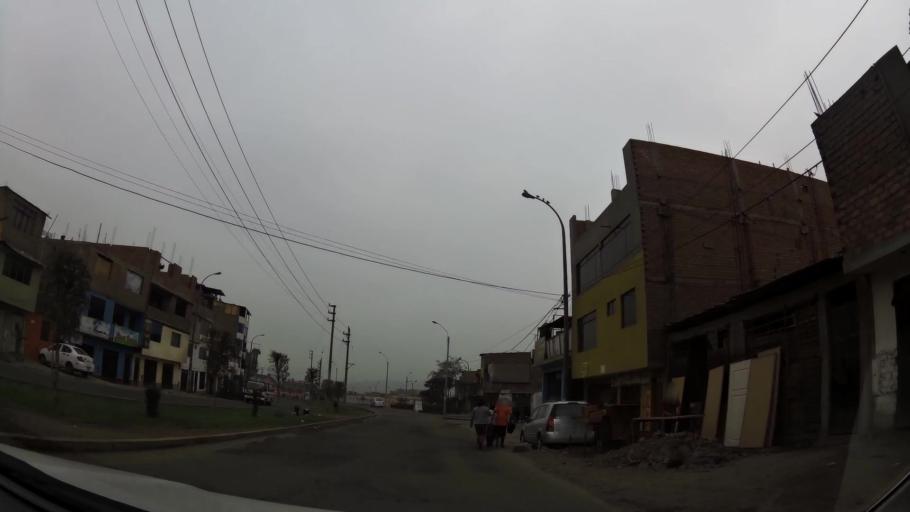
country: PE
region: Lima
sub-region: Lima
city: Urb. Santo Domingo
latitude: -11.9403
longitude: -76.9735
